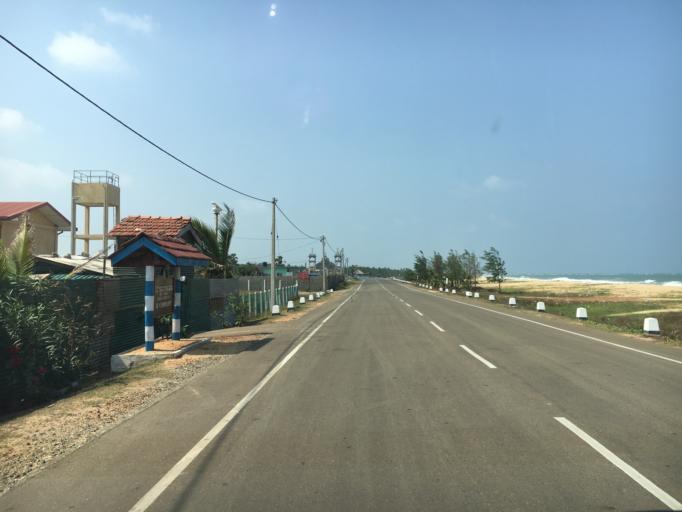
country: LK
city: Padaviya Divisional Secretariat
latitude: 9.2728
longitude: 80.8184
